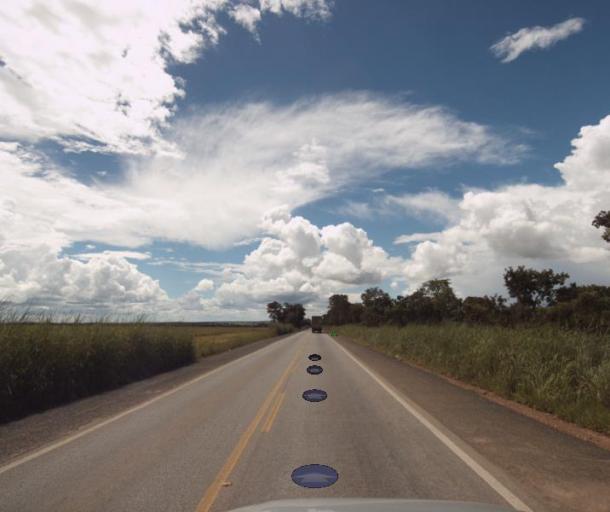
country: BR
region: Goias
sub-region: Uruacu
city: Uruacu
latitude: -14.1105
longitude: -49.1040
